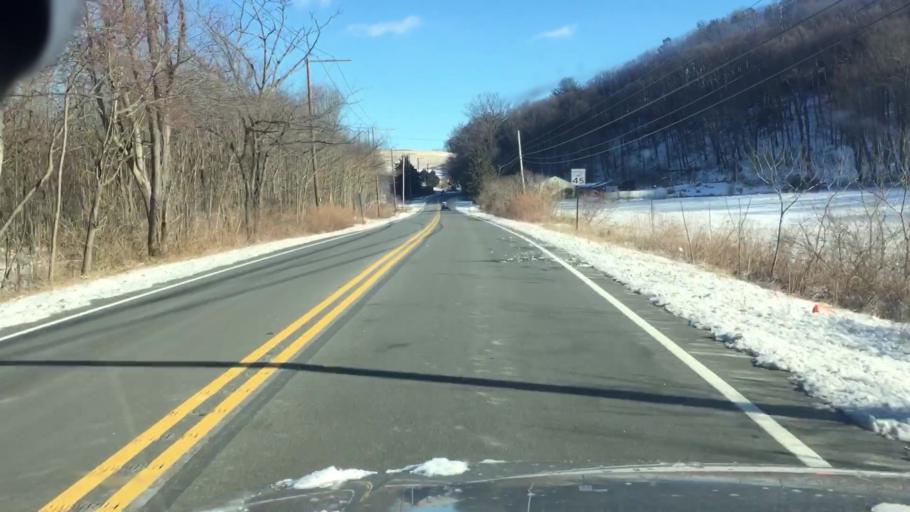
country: US
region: Pennsylvania
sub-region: Luzerne County
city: Nescopeck
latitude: 41.0552
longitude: -76.1804
